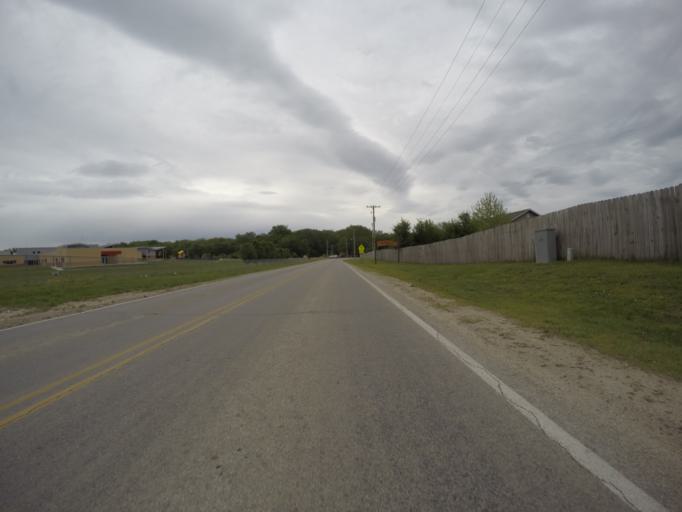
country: US
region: Kansas
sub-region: Pottawatomie County
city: Wamego
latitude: 39.1957
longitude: -96.4298
